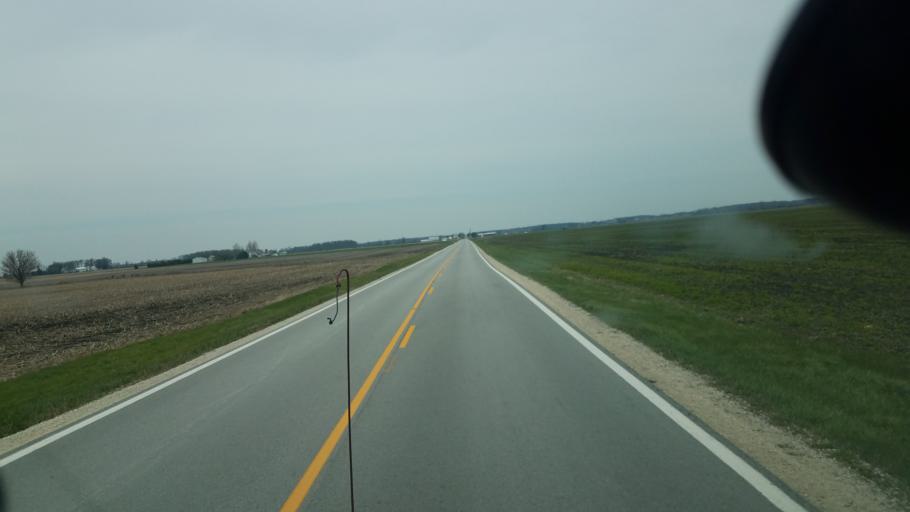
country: US
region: Ohio
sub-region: Wyandot County
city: Carey
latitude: 40.9939
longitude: -83.4779
